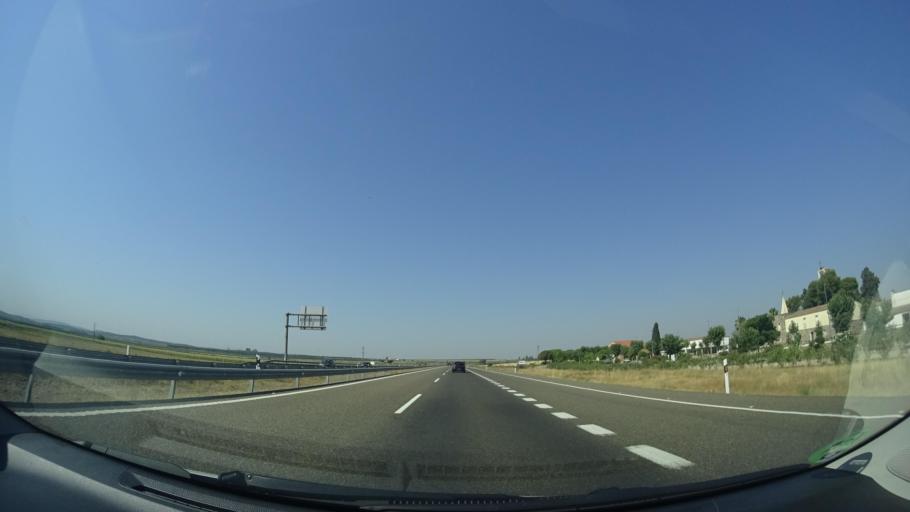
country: ES
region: Extremadura
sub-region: Provincia de Badajoz
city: Santa Amalia
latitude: 39.0744
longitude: -6.0361
